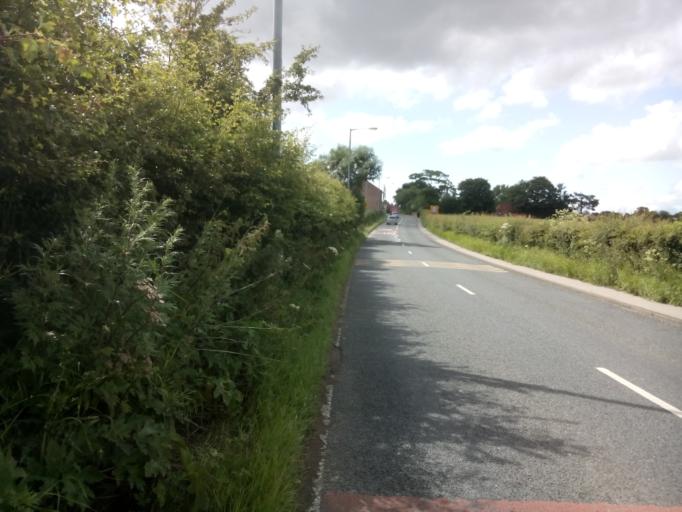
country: GB
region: England
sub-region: County Durham
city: Ushaw Moor
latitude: 54.7697
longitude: -1.6170
